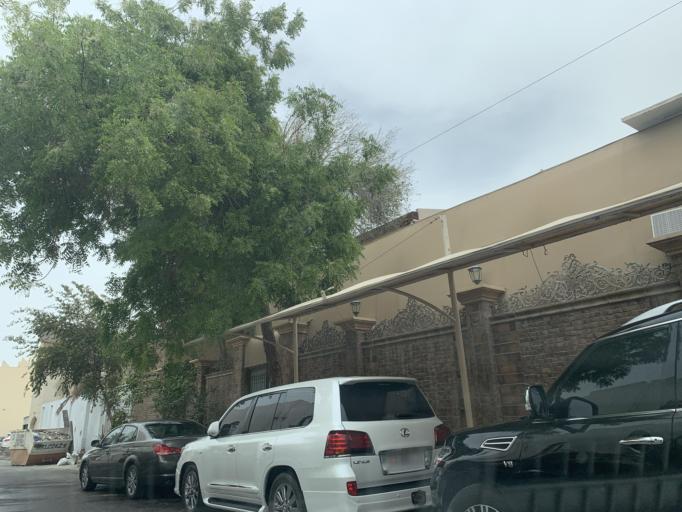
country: BH
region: Northern
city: Ar Rifa'
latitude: 26.1361
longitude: 50.5525
